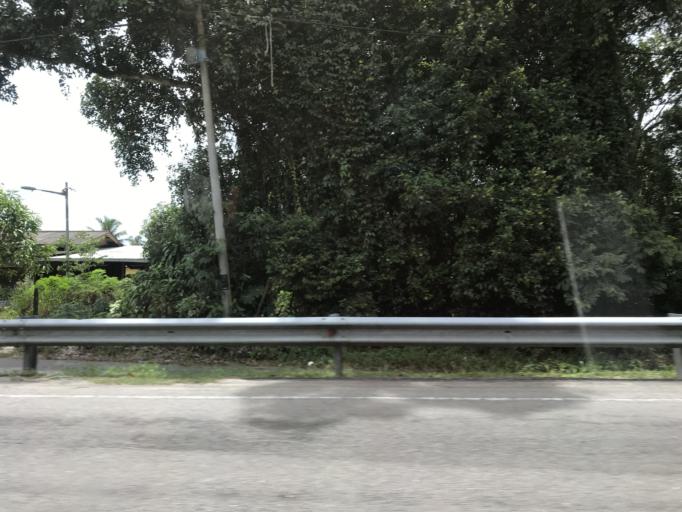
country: MY
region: Kelantan
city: Tumpat
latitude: 6.1782
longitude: 102.1846
